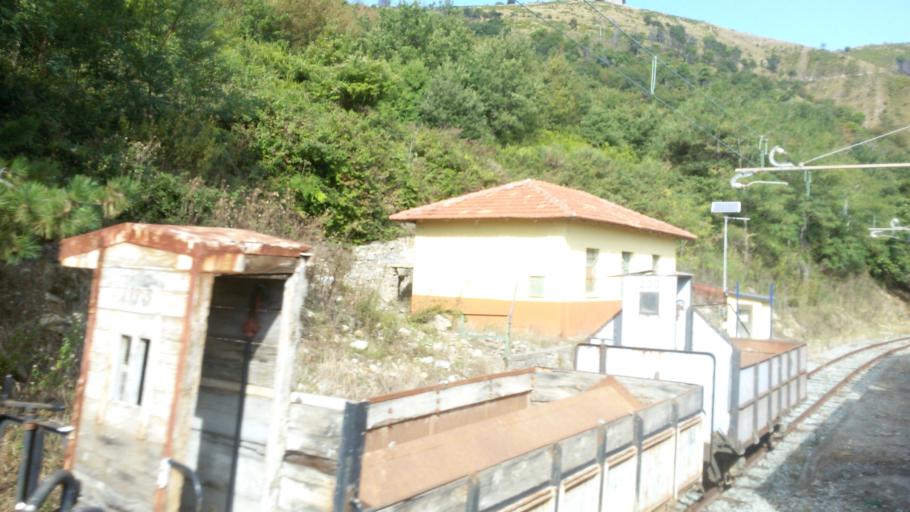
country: IT
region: Liguria
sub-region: Provincia di Genova
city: Genoa
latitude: 44.4425
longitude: 8.9435
